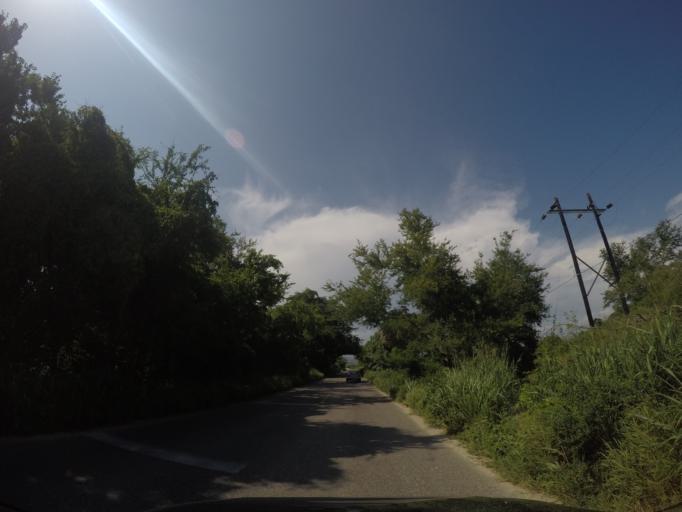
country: MX
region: Oaxaca
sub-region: San Pedro Mixtepec -Dto. 22 -
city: Puerto Escondido
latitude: 15.8959
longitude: -97.1173
